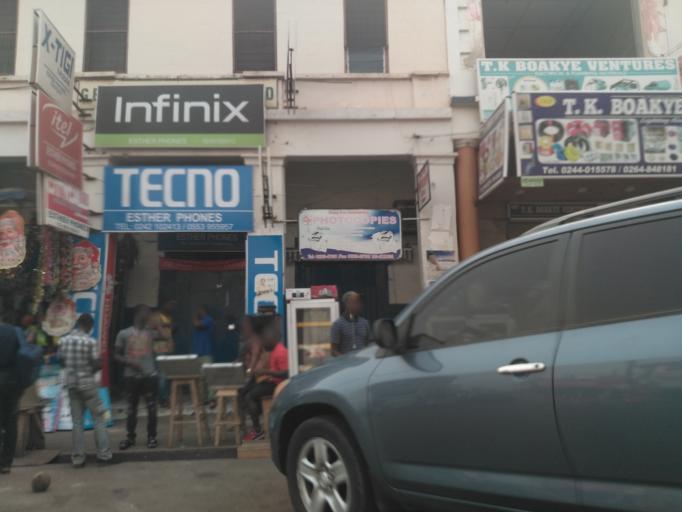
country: GH
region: Ashanti
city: Kumasi
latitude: 6.6928
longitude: -1.6220
